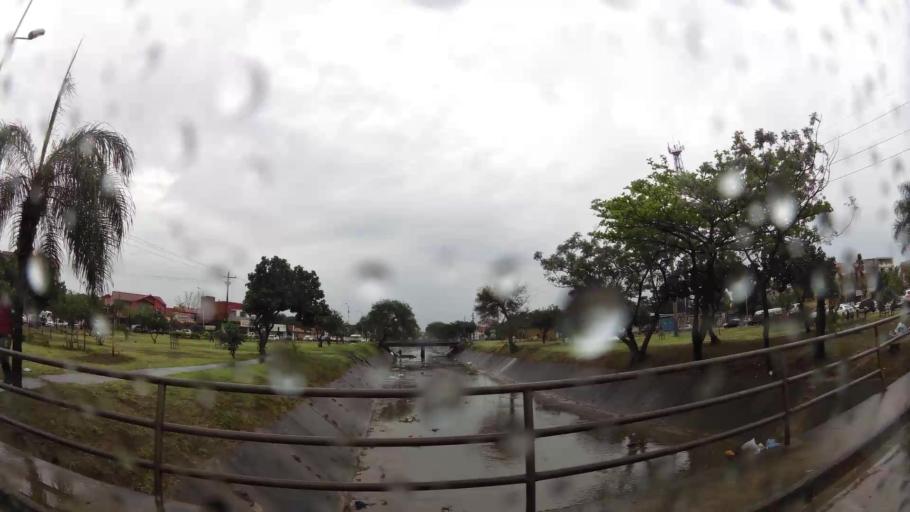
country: BO
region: Santa Cruz
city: Santa Cruz de la Sierra
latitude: -17.7978
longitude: -63.2160
